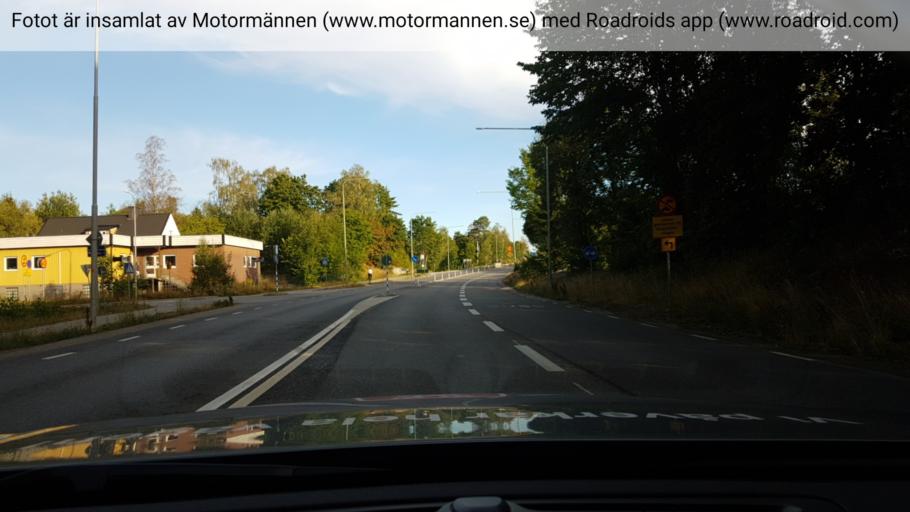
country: SE
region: Stockholm
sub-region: Huddinge Kommun
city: Huddinge
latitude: 59.2351
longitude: 17.9833
